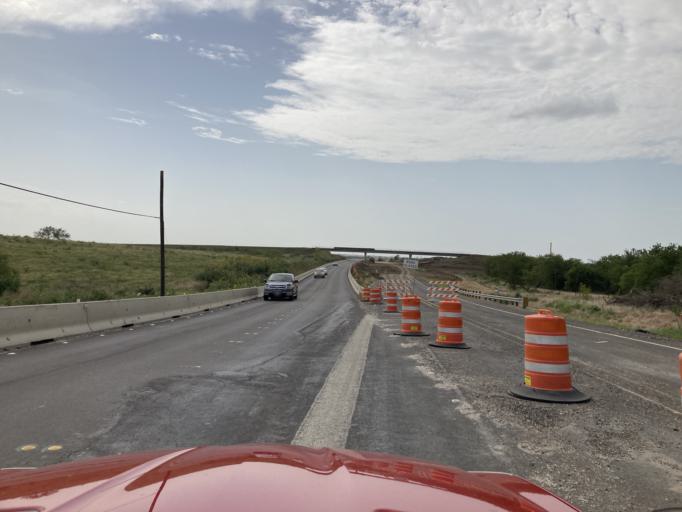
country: US
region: Texas
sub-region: Navarro County
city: Corsicana
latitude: 32.0471
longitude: -96.4169
